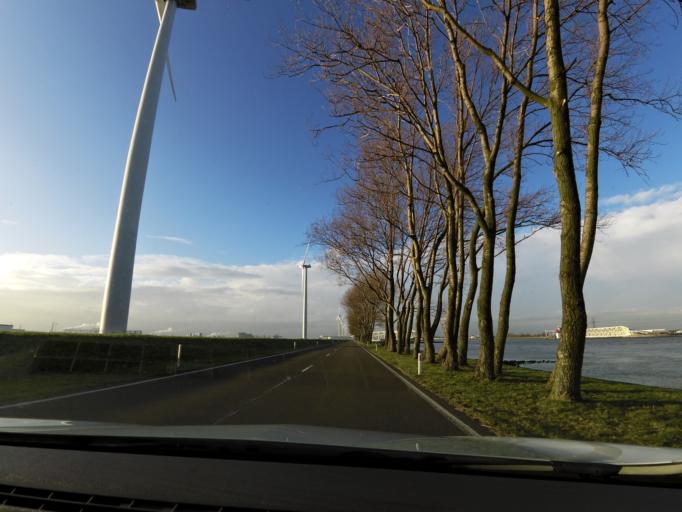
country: NL
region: South Holland
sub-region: Gemeente Westland
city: Maasdijk
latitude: 51.9479
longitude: 4.1692
